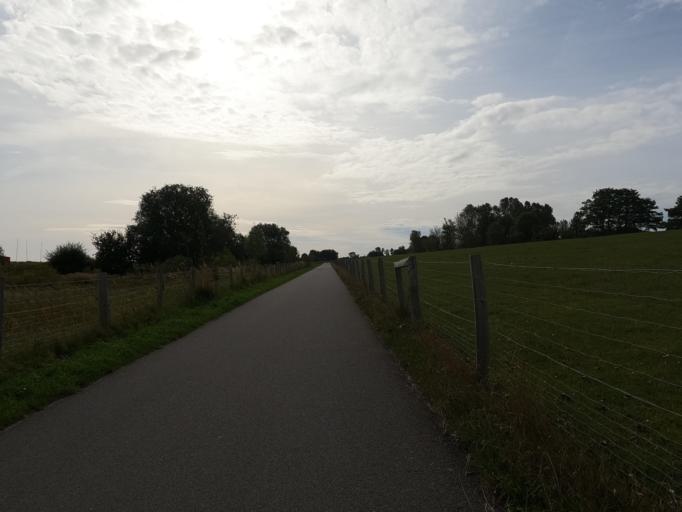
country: DE
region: Schleswig-Holstein
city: Dahme
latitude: 54.2405
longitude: 11.0815
